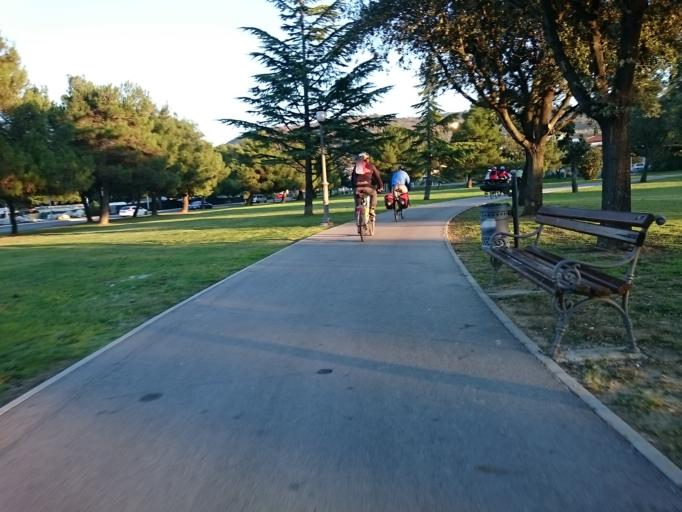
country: SI
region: Izola-Isola
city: Izola
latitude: 45.5388
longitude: 13.6676
